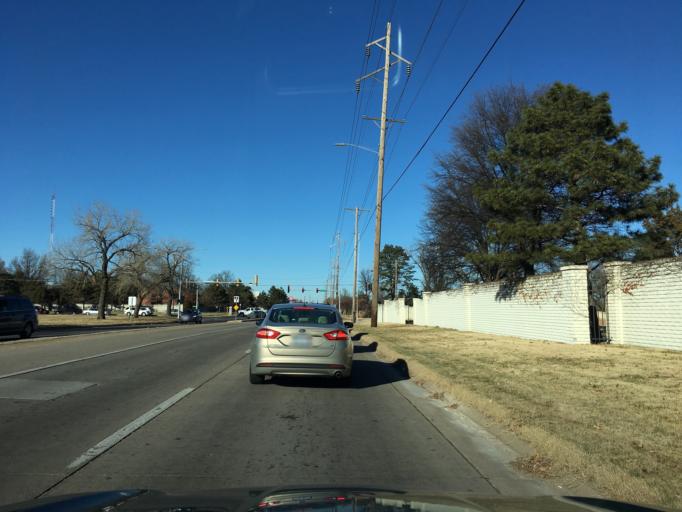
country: US
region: Kansas
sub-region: Sedgwick County
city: Bellaire
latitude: 37.7073
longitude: -97.2446
